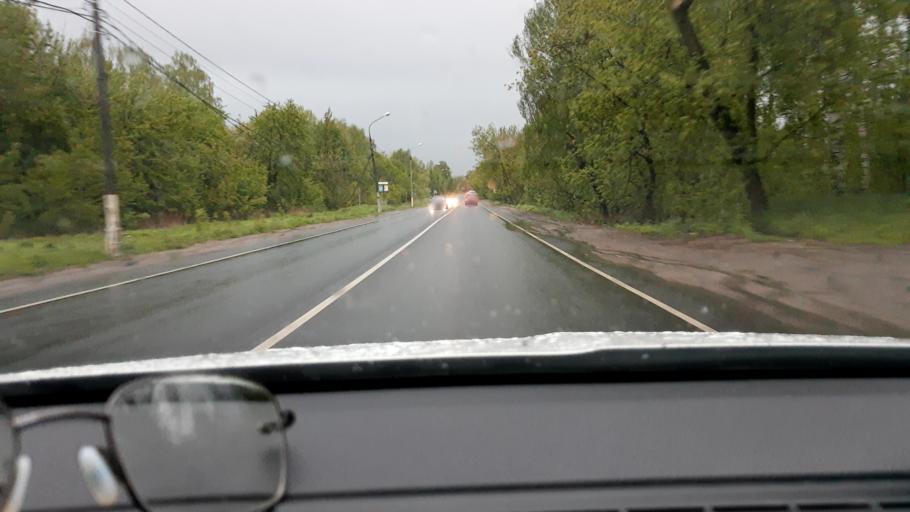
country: RU
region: Moskovskaya
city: Zagoryanskiy
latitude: 55.9281
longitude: 37.9315
